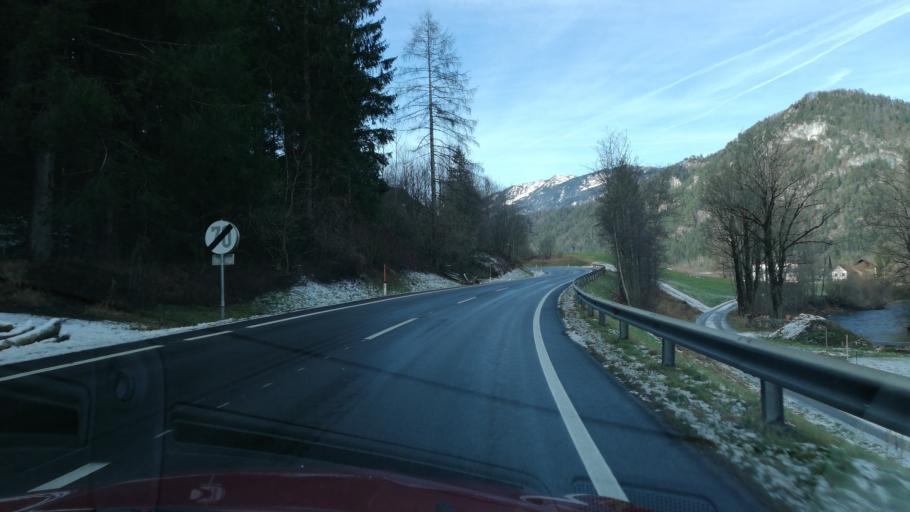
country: AT
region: Upper Austria
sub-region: Politischer Bezirk Kirchdorf an der Krems
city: Rossleithen
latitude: 47.7287
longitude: 14.2937
